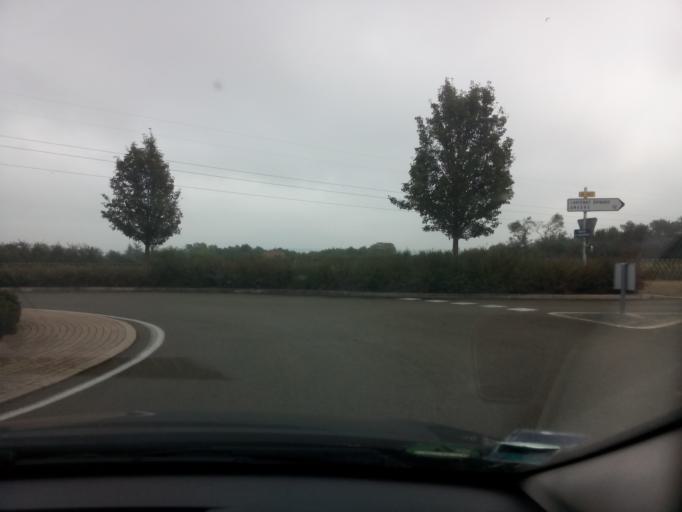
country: FR
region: Pays de la Loire
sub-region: Departement de Maine-et-Loire
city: Soulaire-et-Bourg
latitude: 47.5756
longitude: -0.5547
